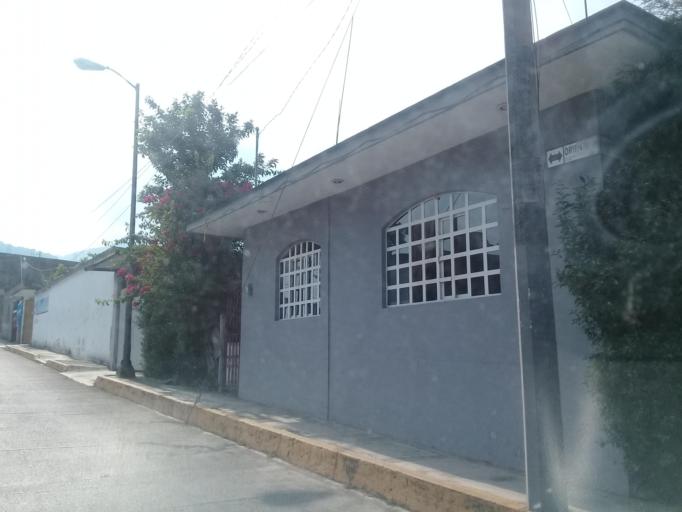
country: MX
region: Veracruz
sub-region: Ixhuatlancillo
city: Union y Progreso
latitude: 18.8669
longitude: -97.1081
